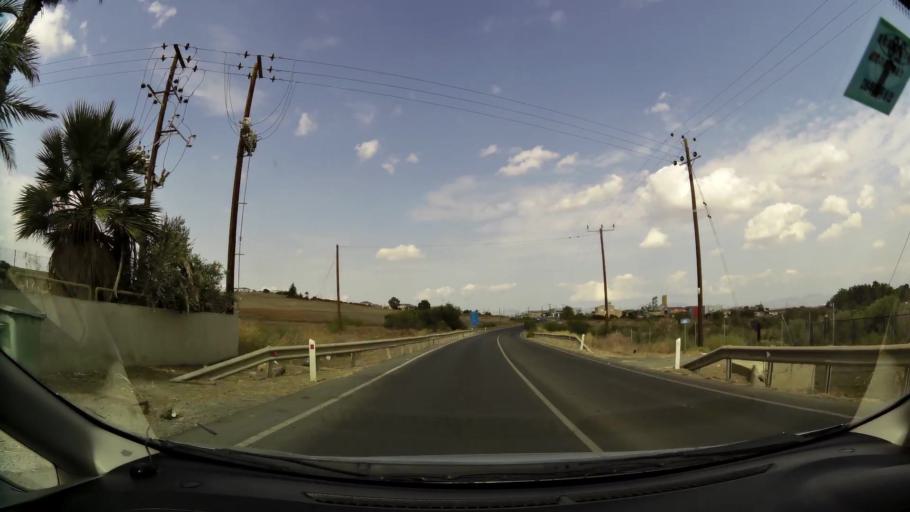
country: CY
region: Lefkosia
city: Tseri
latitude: 35.0930
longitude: 33.3268
